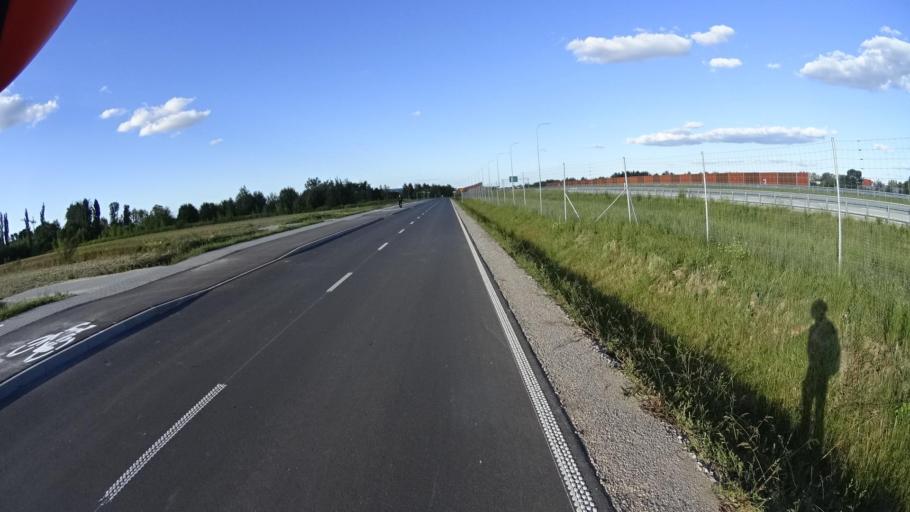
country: PL
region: Masovian Voivodeship
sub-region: Powiat piaseczynski
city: Mysiadlo
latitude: 52.1097
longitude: 20.9759
